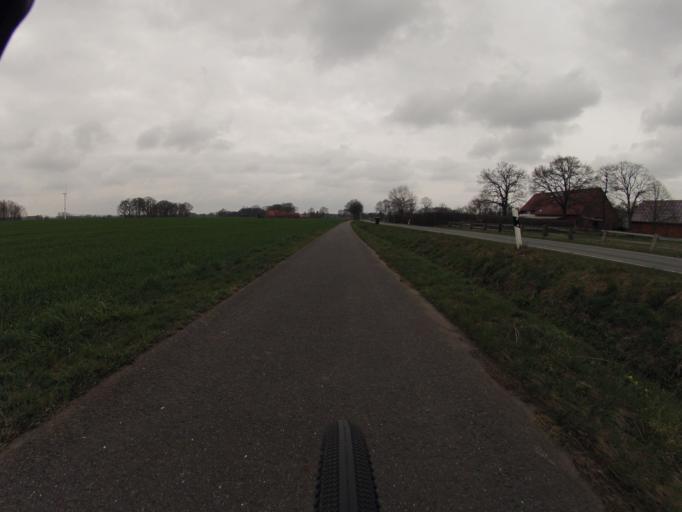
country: DE
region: North Rhine-Westphalia
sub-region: Regierungsbezirk Munster
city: Mettingen
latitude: 52.3445
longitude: 7.8090
